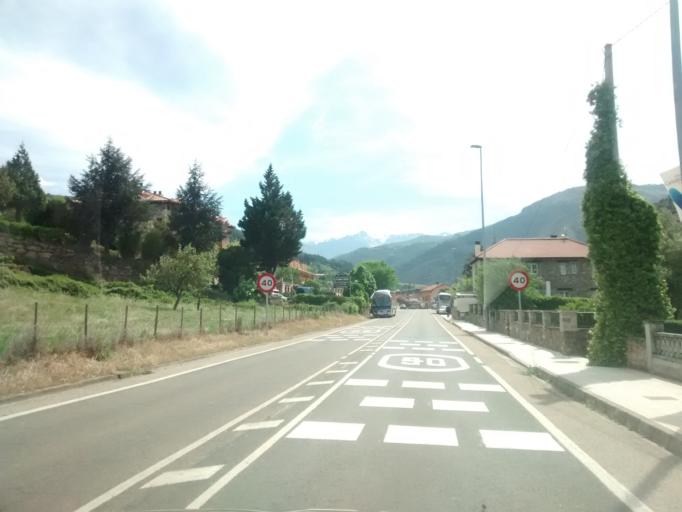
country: ES
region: Cantabria
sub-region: Provincia de Cantabria
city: Potes
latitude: 43.1641
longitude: -4.6091
